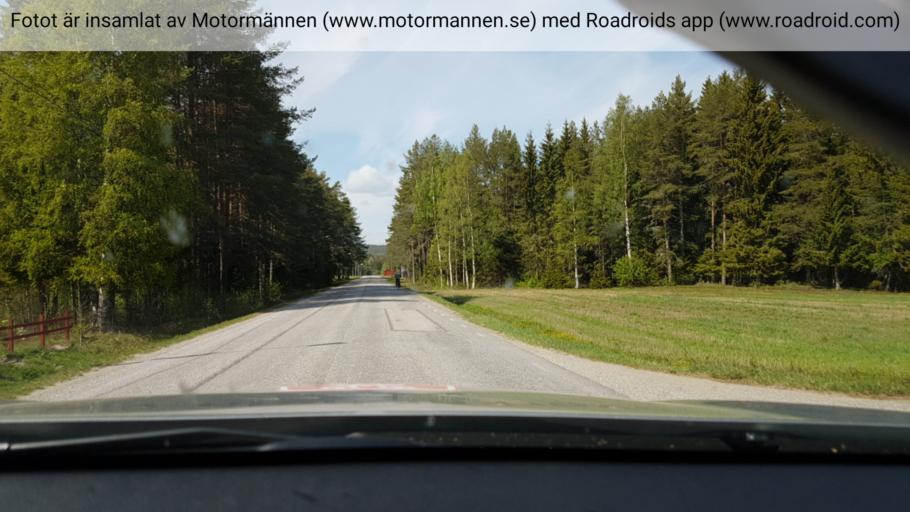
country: SE
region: Vaesterbotten
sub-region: Umea Kommun
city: Roback
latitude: 63.8306
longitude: 20.1122
